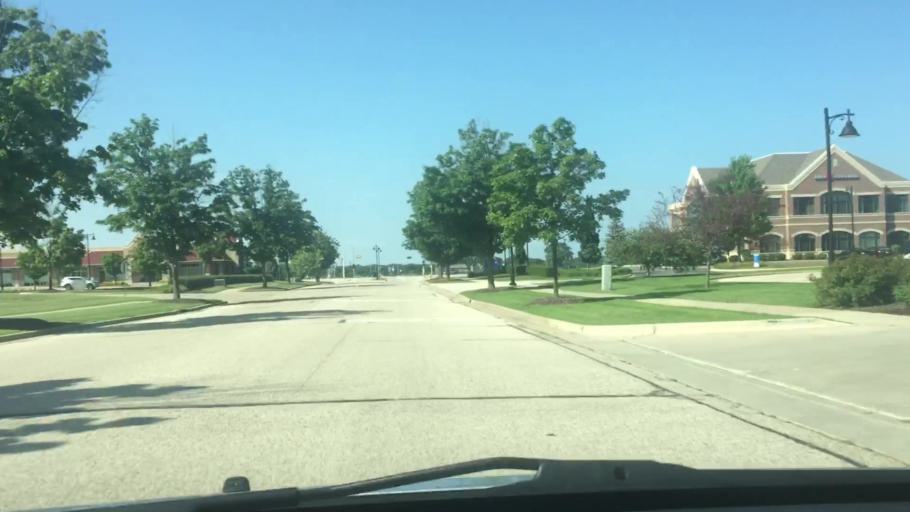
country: US
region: Wisconsin
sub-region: Waukesha County
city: Oconomowoc
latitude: 43.0743
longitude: -88.4674
